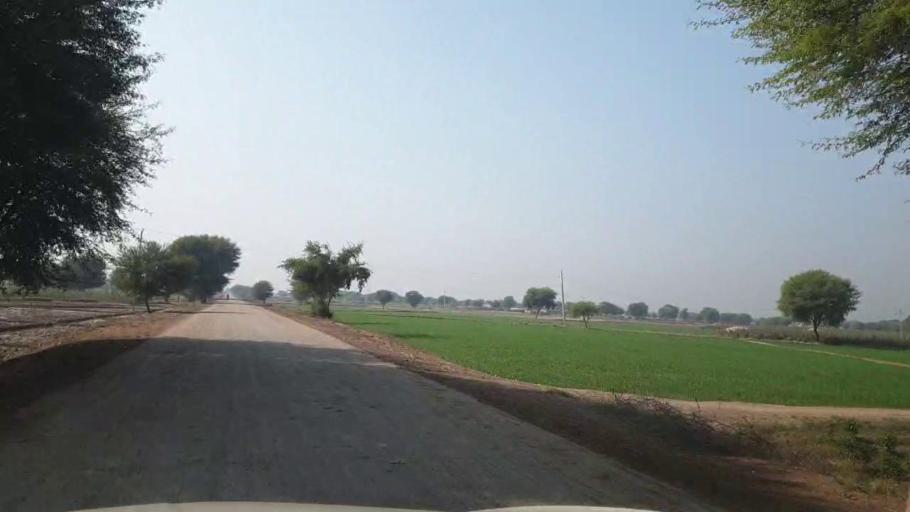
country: PK
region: Sindh
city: Bhan
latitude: 26.5184
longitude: 67.8037
